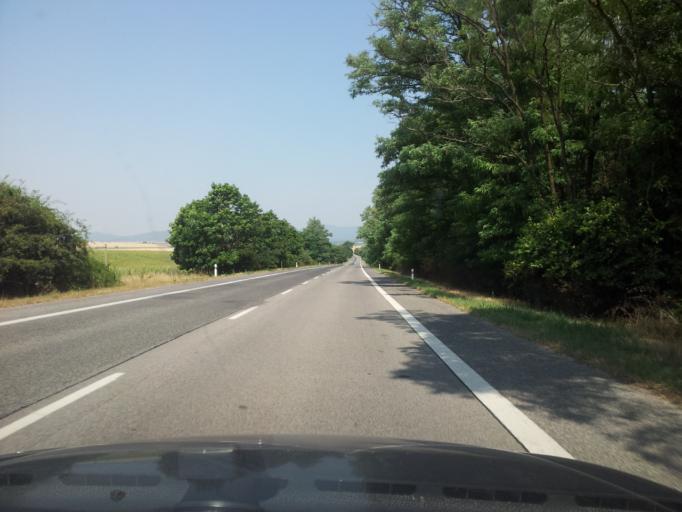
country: SK
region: Nitriansky
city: Zlate Moravce
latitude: 48.3655
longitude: 18.4473
